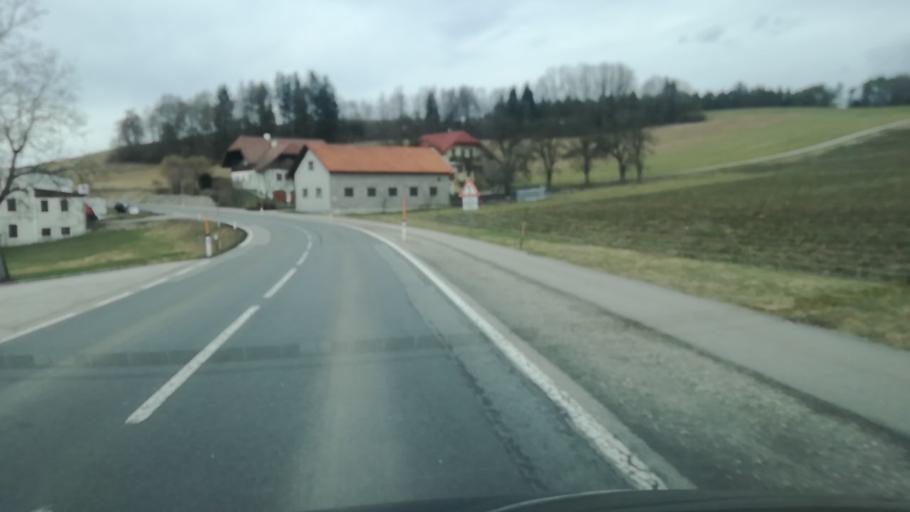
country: AT
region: Upper Austria
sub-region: Politischer Bezirk Vocklabruck
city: Frankenburg
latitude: 48.0793
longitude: 13.4887
